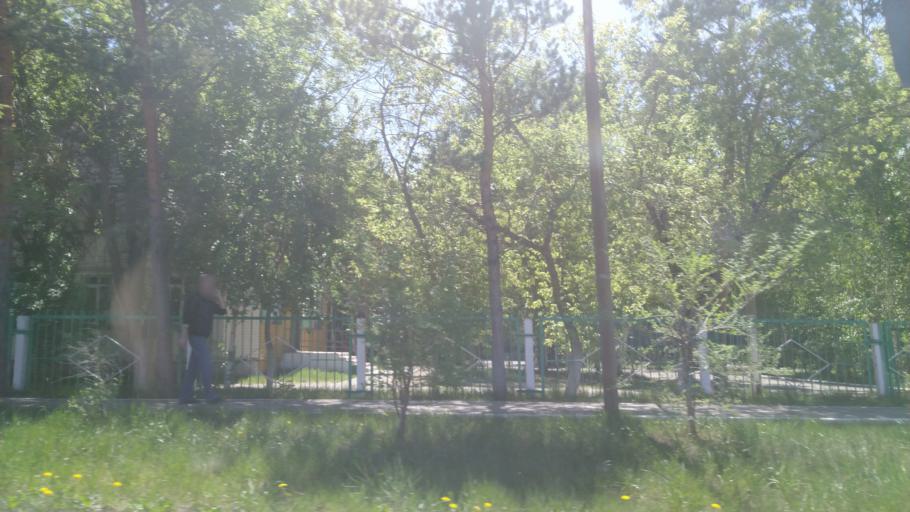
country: KZ
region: Pavlodar
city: Pavlodar
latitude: 52.2921
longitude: 77.0073
